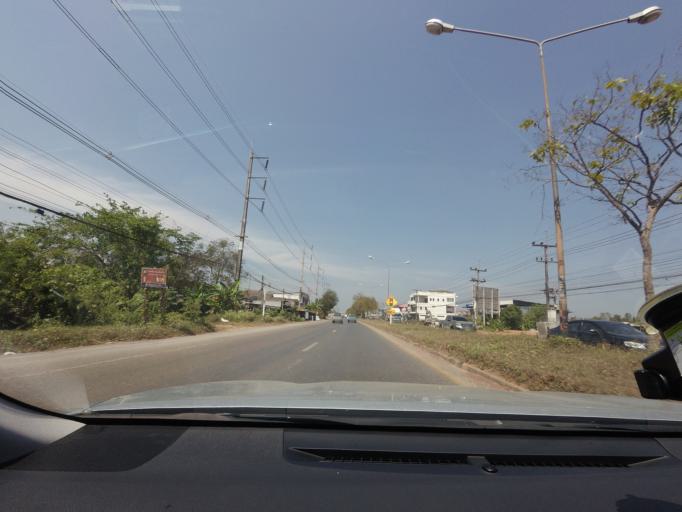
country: TH
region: Surat Thani
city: Surat Thani
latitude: 9.1477
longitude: 99.3978
